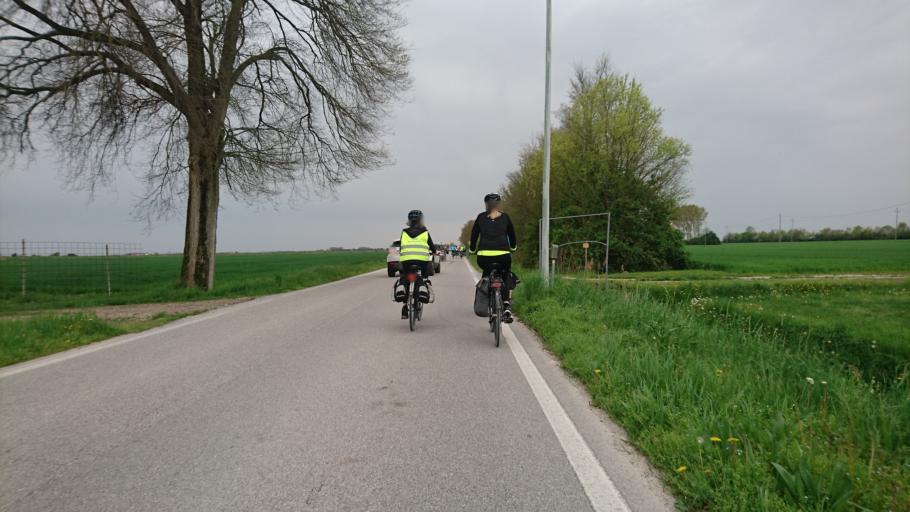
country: IT
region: Veneto
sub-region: Provincia di Venezia
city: Lugugnana
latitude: 45.6822
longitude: 12.9475
